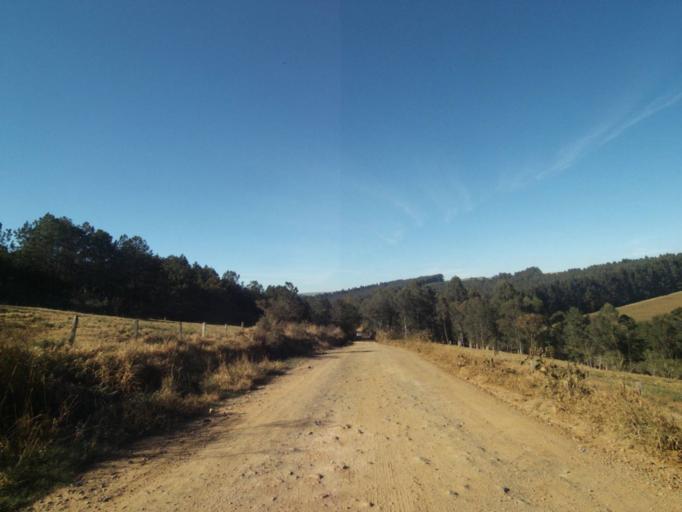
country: BR
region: Parana
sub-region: Tibagi
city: Tibagi
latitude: -24.5297
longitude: -50.3787
